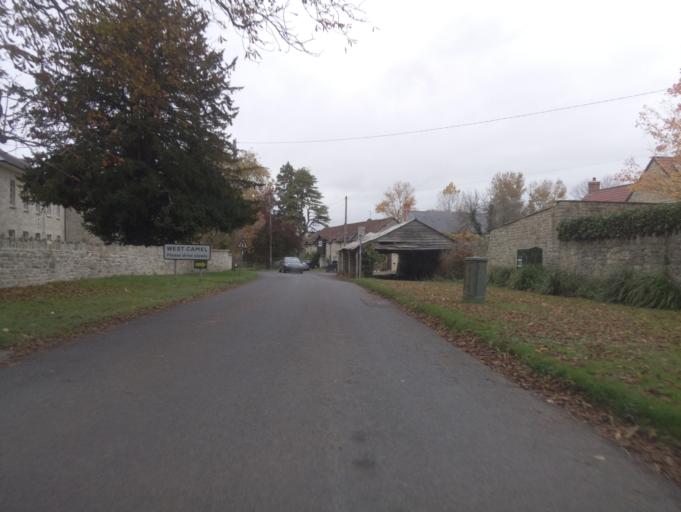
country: GB
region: England
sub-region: Somerset
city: Ilchester
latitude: 51.0187
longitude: -2.6010
